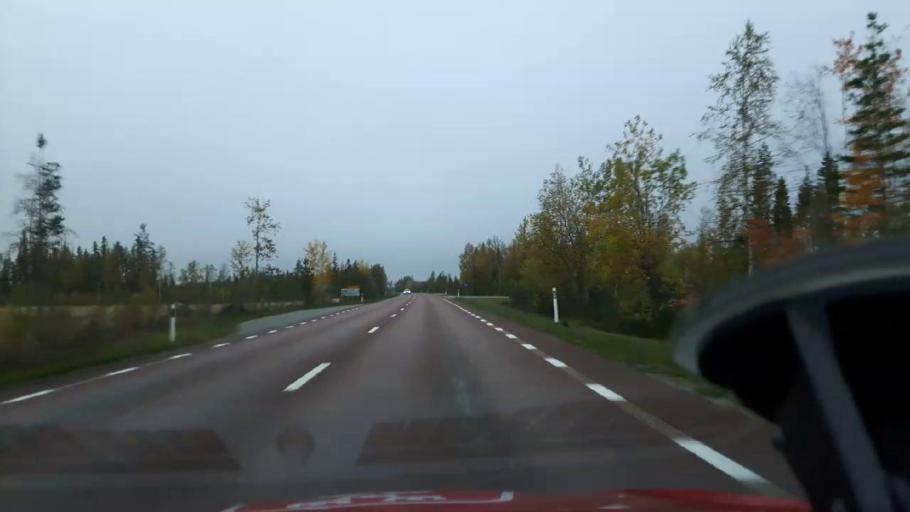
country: SE
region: Jaemtland
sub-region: Bergs Kommun
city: Hoverberg
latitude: 62.5285
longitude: 14.4468
